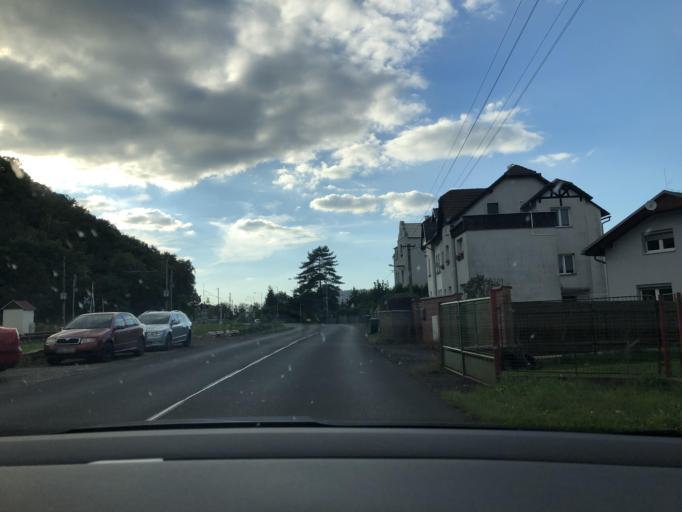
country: CZ
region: Ustecky
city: Velke Brezno
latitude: 50.6612
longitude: 14.0905
